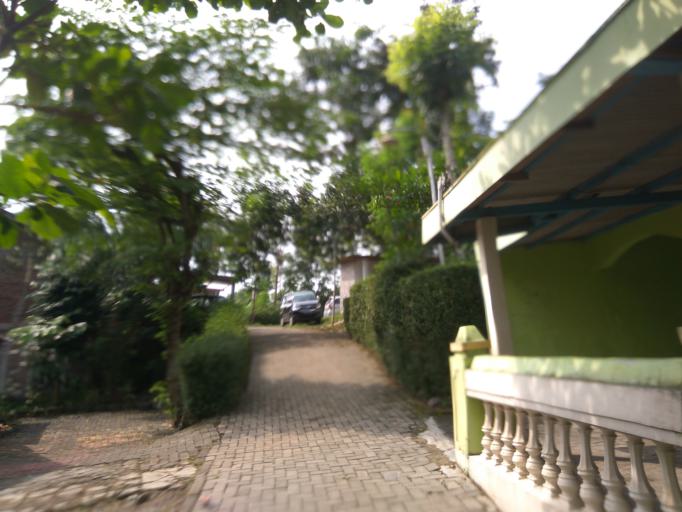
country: ID
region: Central Java
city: Semarang
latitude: -7.0371
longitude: 110.4062
